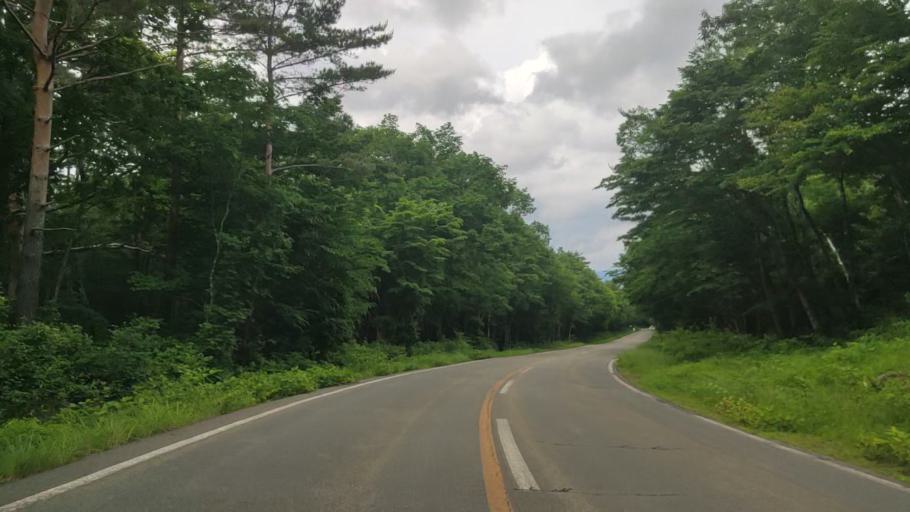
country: JP
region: Yamanashi
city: Fujikawaguchiko
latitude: 35.4442
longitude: 138.7479
